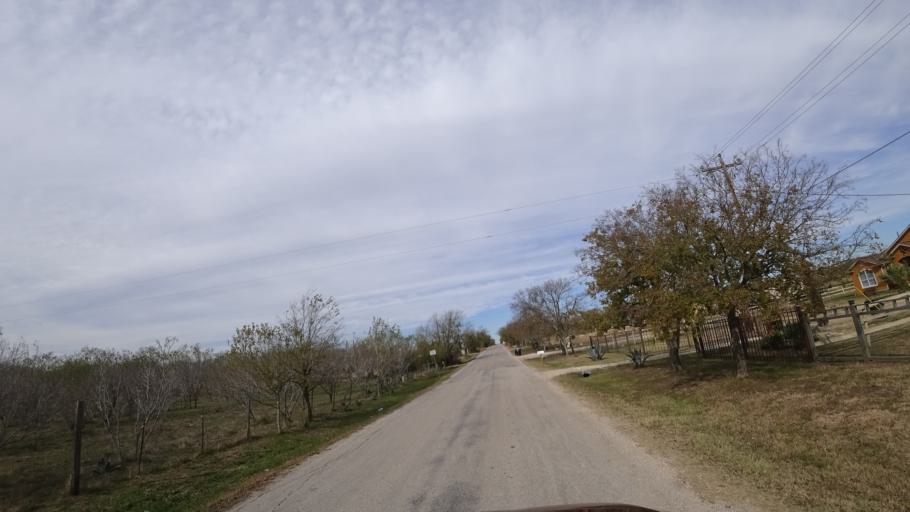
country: US
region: Texas
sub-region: Travis County
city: Garfield
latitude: 30.1182
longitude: -97.5923
